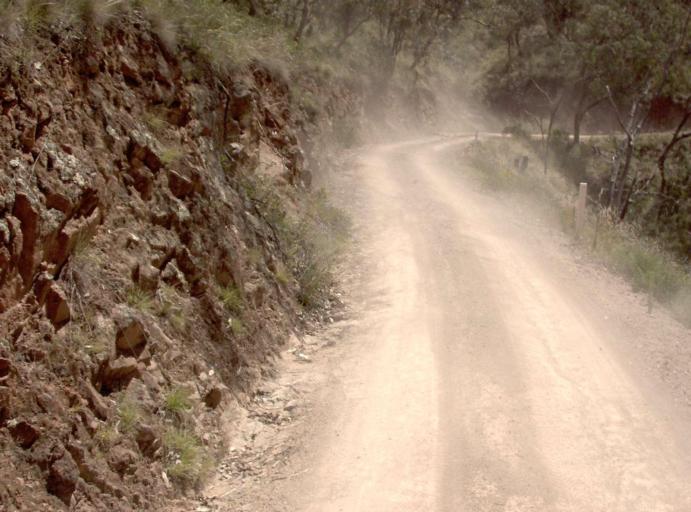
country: AU
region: New South Wales
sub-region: Snowy River
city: Jindabyne
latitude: -37.0865
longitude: 148.3603
